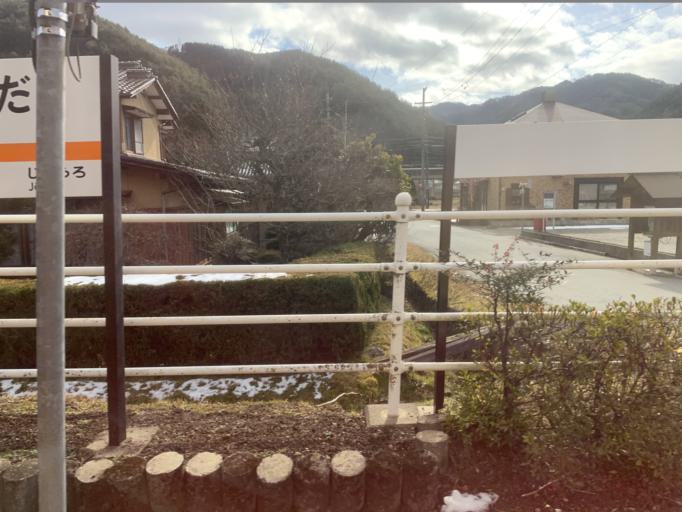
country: JP
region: Gifu
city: Takayama
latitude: 35.9286
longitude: 137.2362
